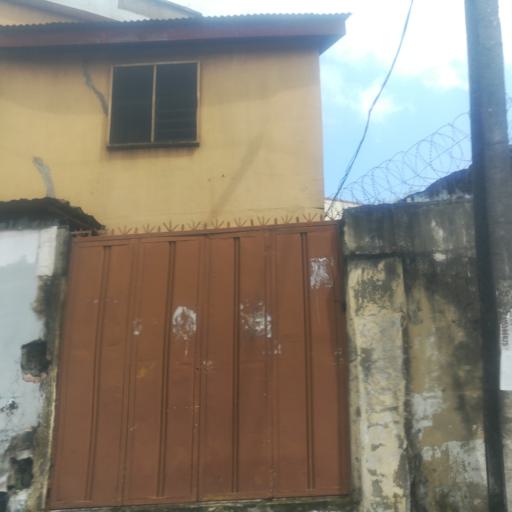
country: NG
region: Lagos
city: Ojota
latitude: 6.6026
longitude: 3.3922
